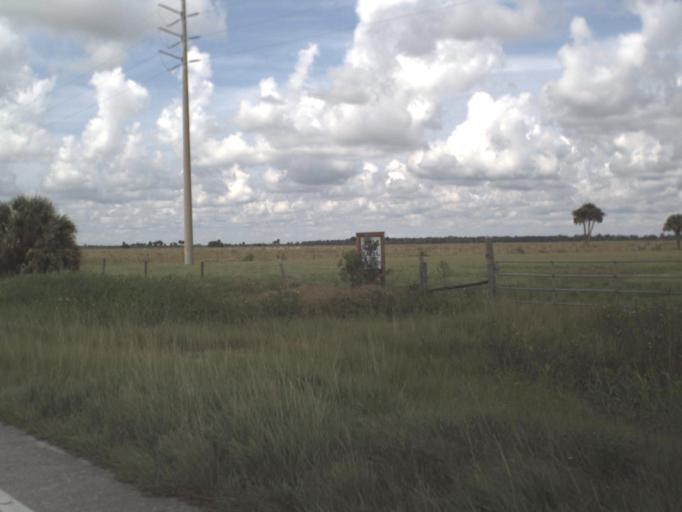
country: US
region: Florida
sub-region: Okeechobee County
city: Okeechobee
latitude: 27.2436
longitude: -80.9107
